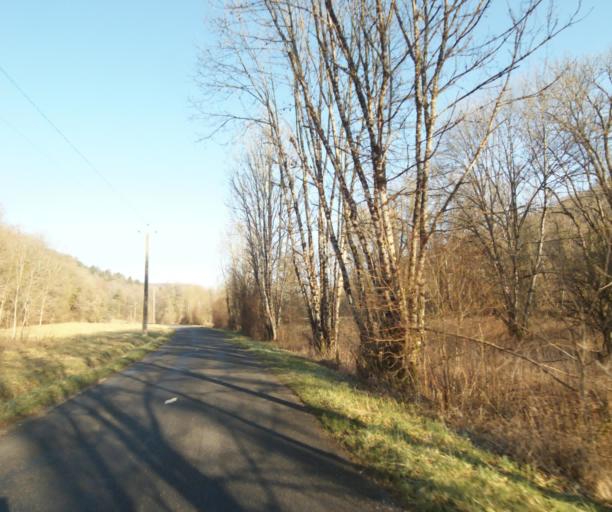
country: FR
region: Champagne-Ardenne
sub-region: Departement de la Haute-Marne
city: Chevillon
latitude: 48.4961
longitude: 5.1507
